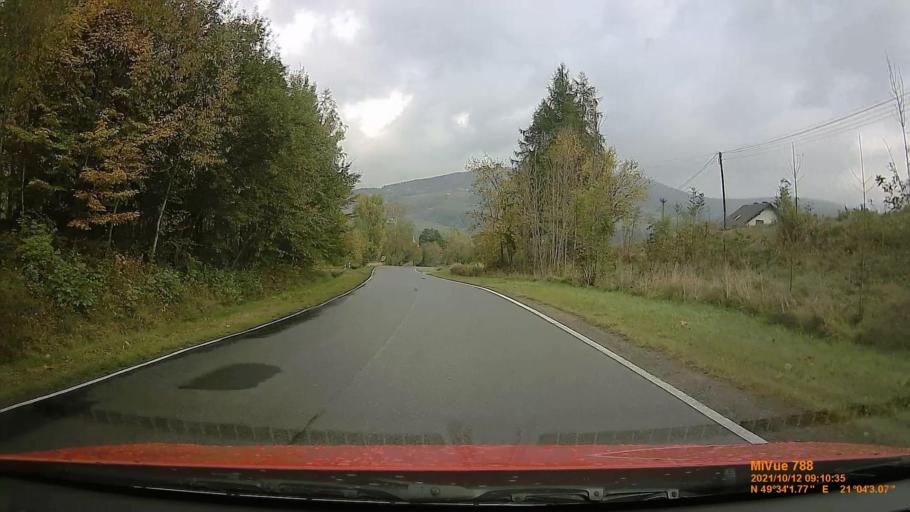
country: PL
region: Lesser Poland Voivodeship
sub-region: Powiat gorlicki
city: Ropa
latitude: 49.5673
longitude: 21.0675
